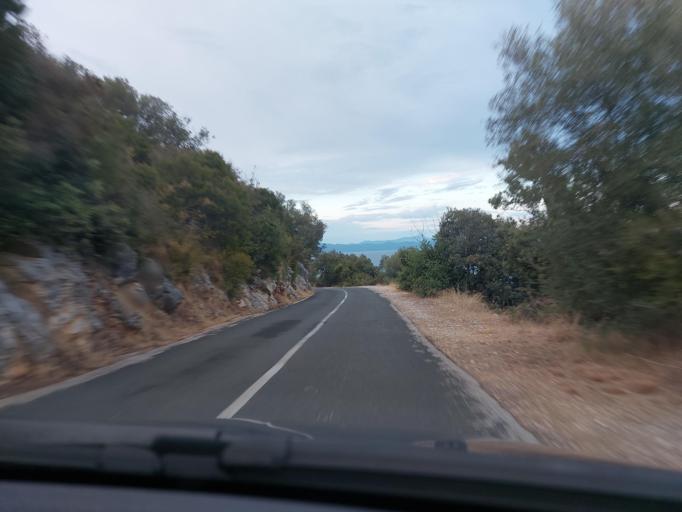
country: HR
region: Dubrovacko-Neretvanska
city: Smokvica
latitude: 42.7712
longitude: 16.8780
